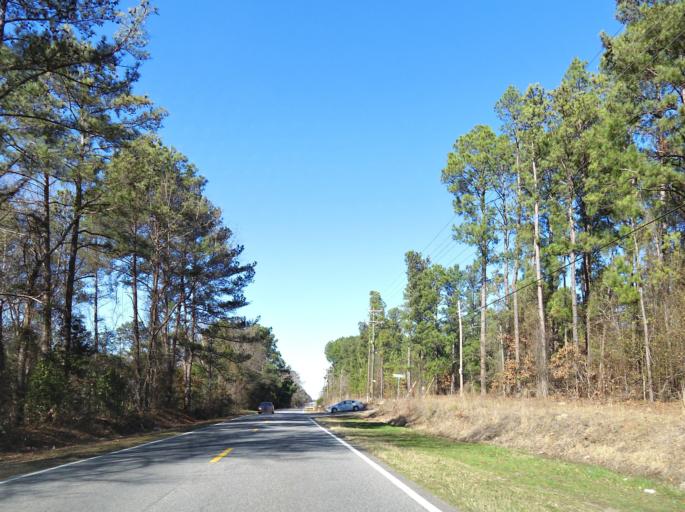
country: US
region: Georgia
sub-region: Bibb County
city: West Point
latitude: 32.7663
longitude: -83.7736
